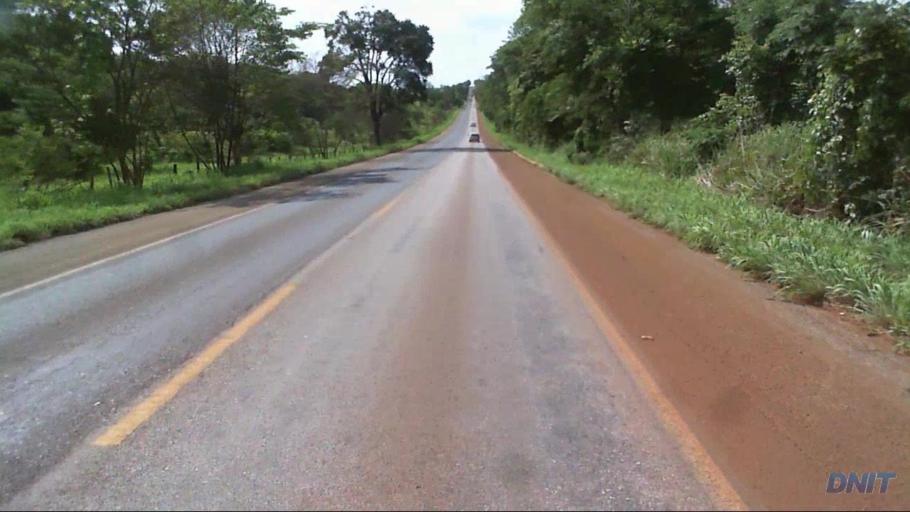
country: BR
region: Goias
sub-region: Barro Alto
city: Barro Alto
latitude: -15.0075
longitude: -48.9023
